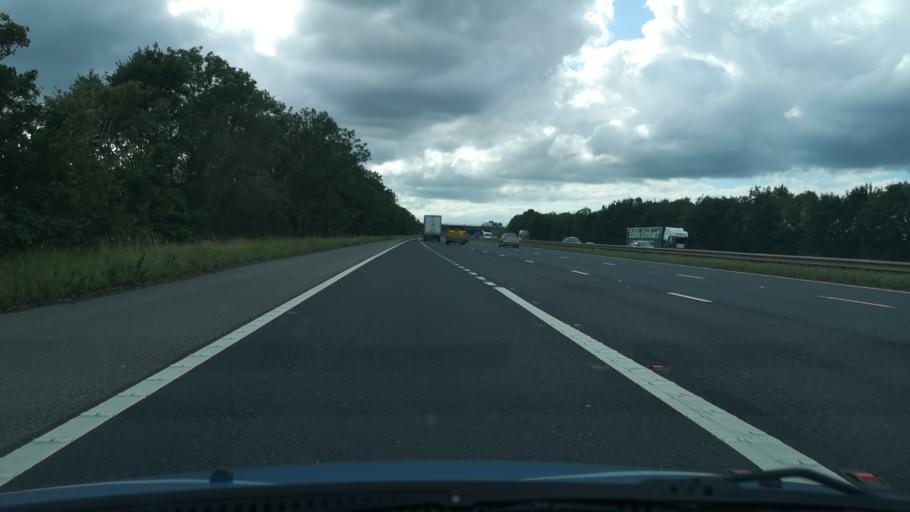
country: GB
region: England
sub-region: East Riding of Yorkshire
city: Rawcliffe
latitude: 53.6814
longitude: -0.9817
